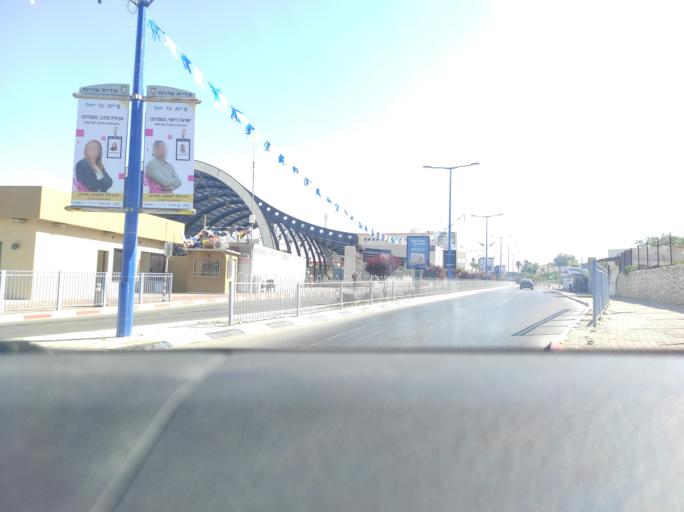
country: IL
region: Southern District
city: Sederot
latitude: 31.5235
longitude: 34.5952
